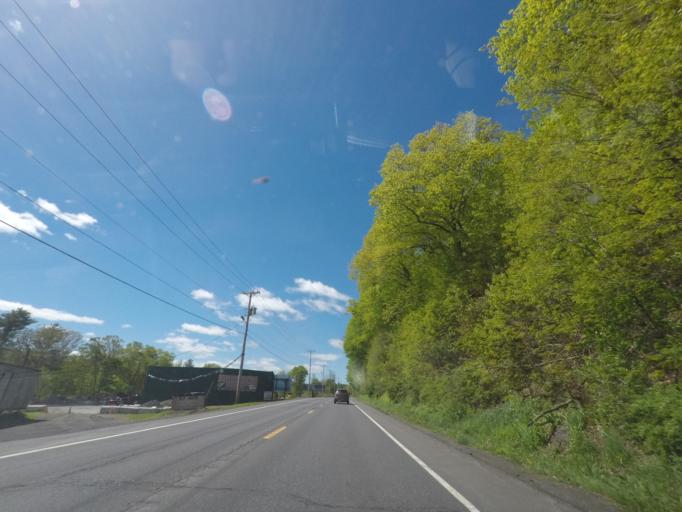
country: US
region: New York
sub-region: Ulster County
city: Lake Katrine
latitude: 42.0104
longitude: -73.9813
